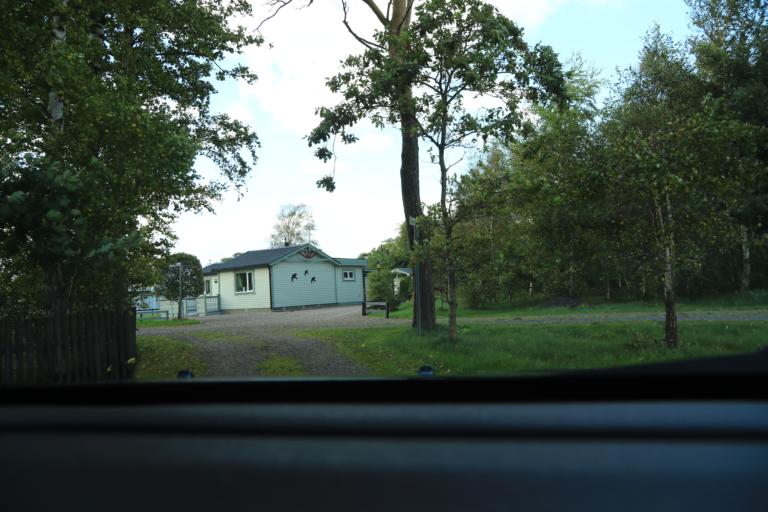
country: SE
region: Halland
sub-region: Varbergs Kommun
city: Tvaaker
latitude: 57.0094
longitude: 12.3557
